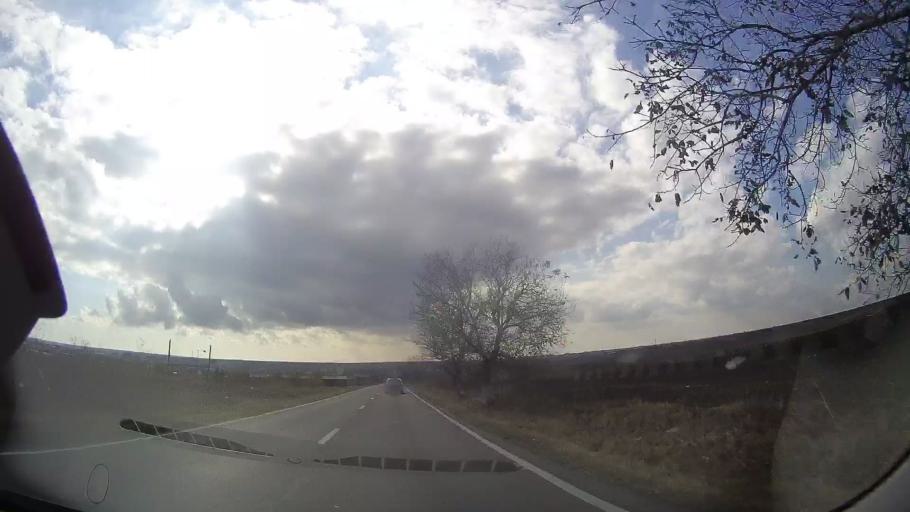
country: RO
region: Constanta
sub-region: Oras Techirghiol
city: Techirghiol
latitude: 44.0693
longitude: 28.5955
